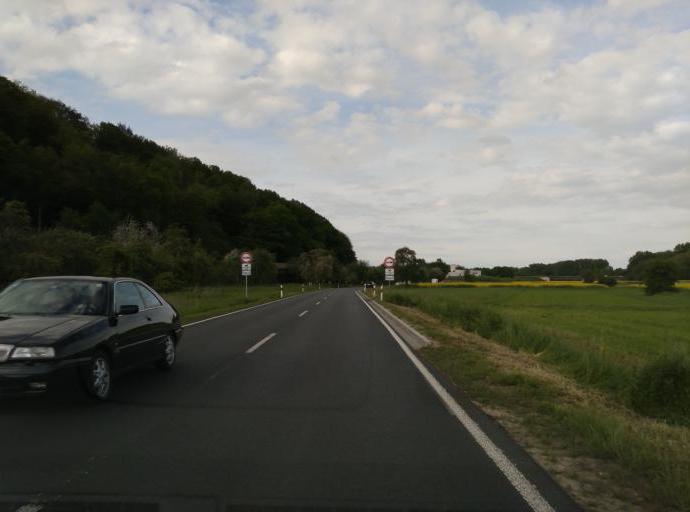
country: DE
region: Baden-Wuerttemberg
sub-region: Regierungsbezirk Stuttgart
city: Neckartenzlingen
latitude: 48.6002
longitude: 9.2491
